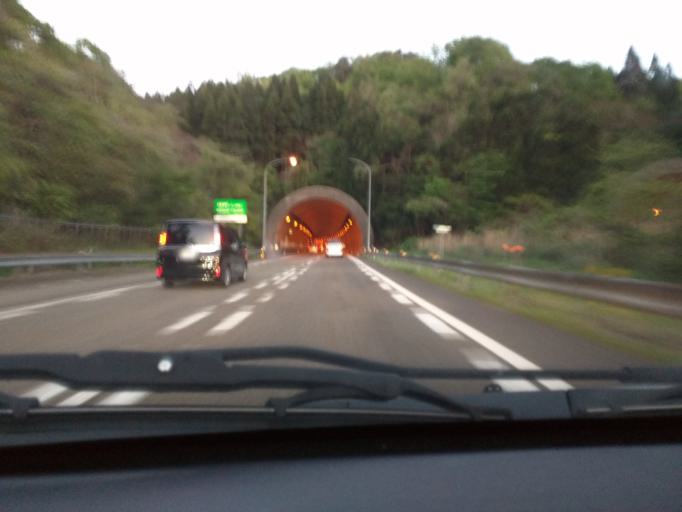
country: JP
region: Niigata
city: Kashiwazaki
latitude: 37.3438
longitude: 138.5147
